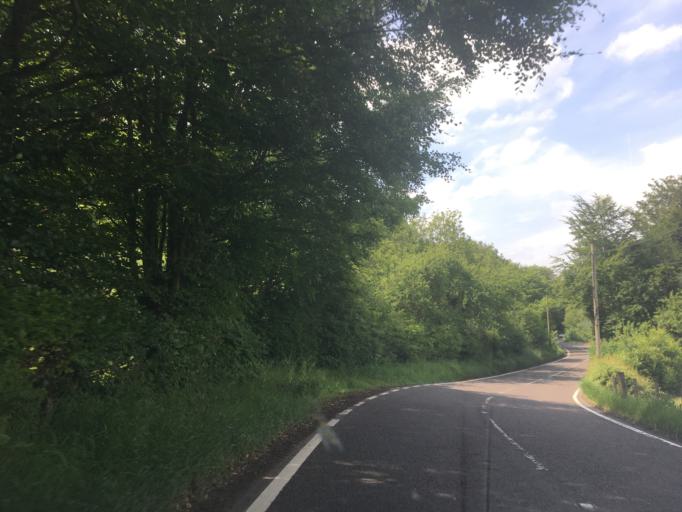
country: GB
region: Scotland
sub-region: South Lanarkshire
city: Dalserf
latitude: 55.7170
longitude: -3.8935
